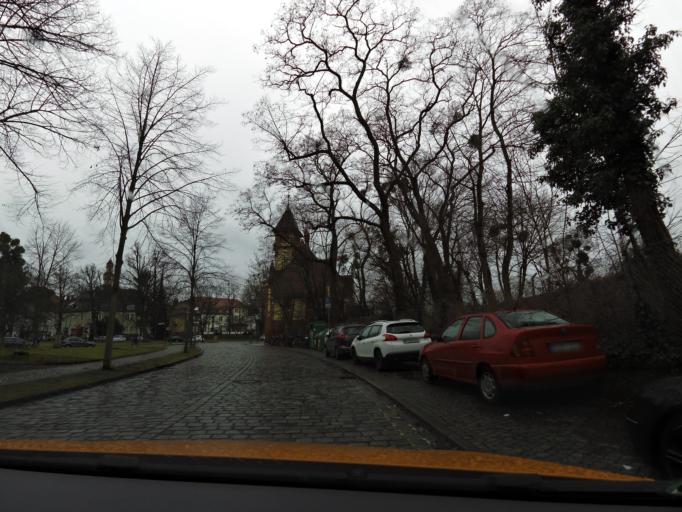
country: DE
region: Berlin
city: Nikolassee
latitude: 52.4315
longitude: 13.1944
